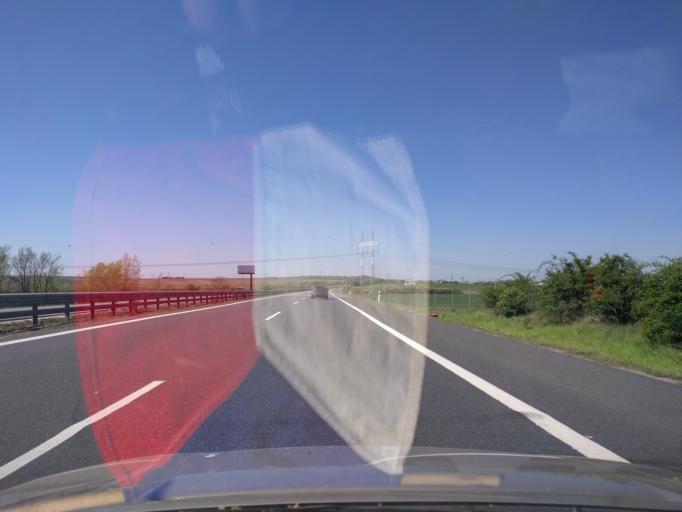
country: CZ
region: Central Bohemia
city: Prerov nad Labem
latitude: 50.1355
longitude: 14.8219
